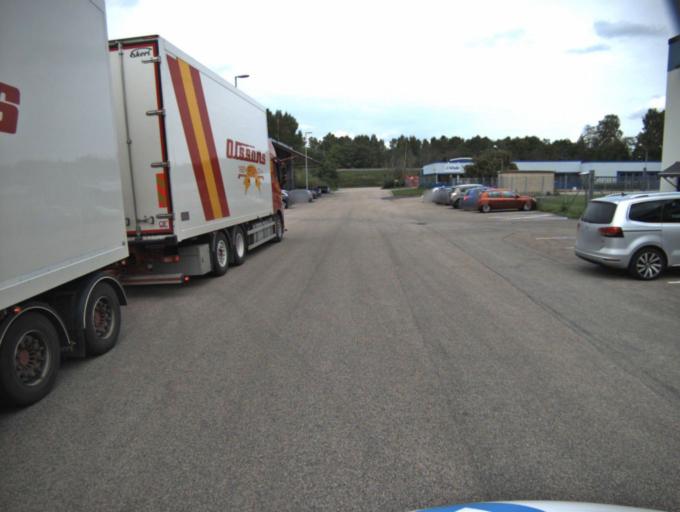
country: SE
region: Vaestra Goetaland
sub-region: Ulricehamns Kommun
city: Ulricehamn
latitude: 57.8015
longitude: 13.4136
